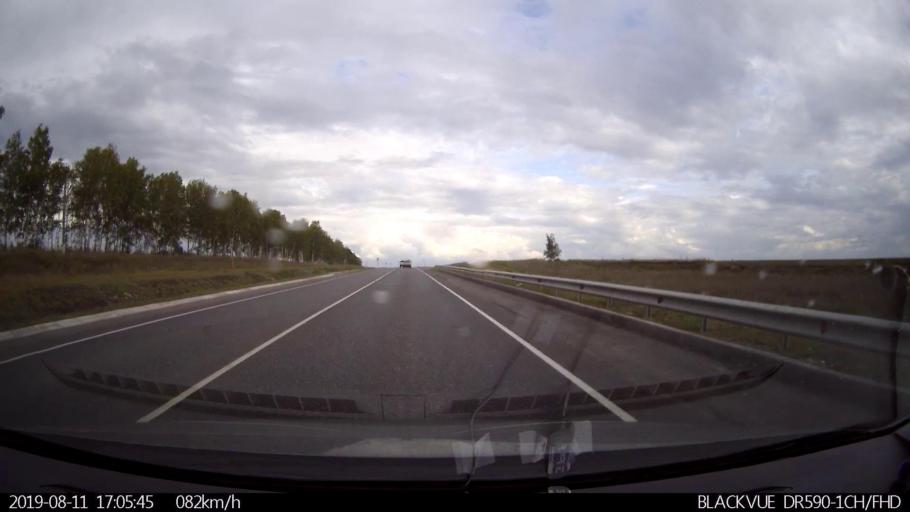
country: RU
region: Ulyanovsk
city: Mayna
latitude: 54.2970
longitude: 47.7923
